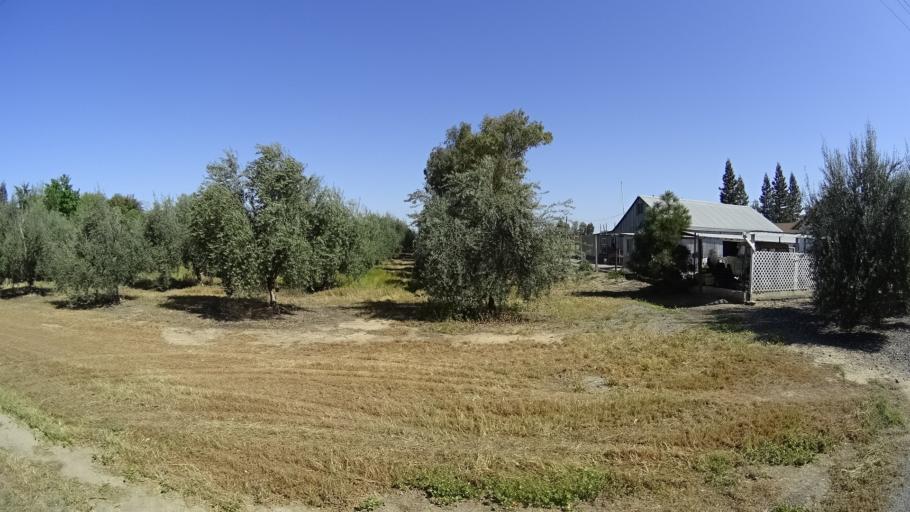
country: US
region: California
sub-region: Glenn County
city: Orland
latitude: 39.7220
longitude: -122.1840
